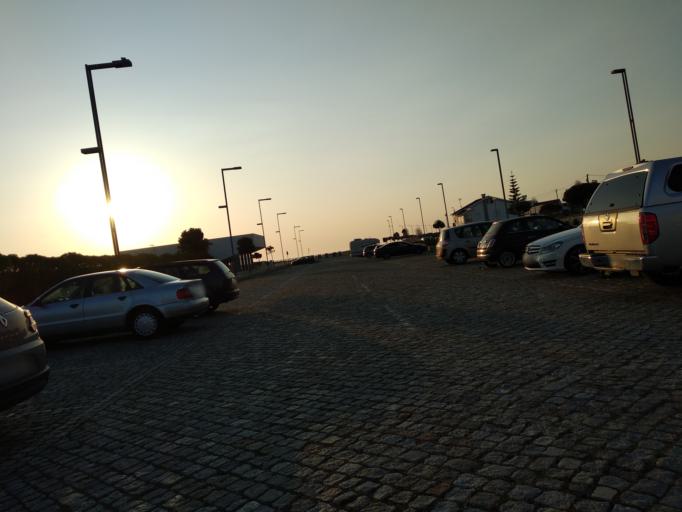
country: PT
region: Viana do Castelo
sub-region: Caminha
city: Vila Praia de Ancora
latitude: 41.8167
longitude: -8.8688
